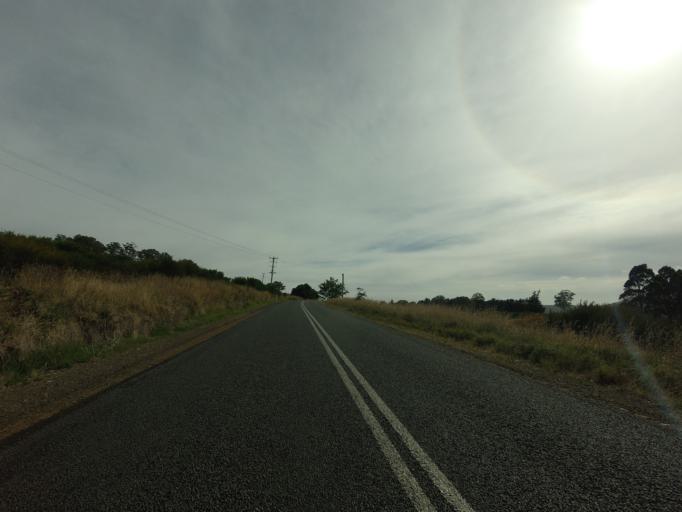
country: AU
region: Tasmania
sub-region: Brighton
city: Bridgewater
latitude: -42.3815
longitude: 147.4244
